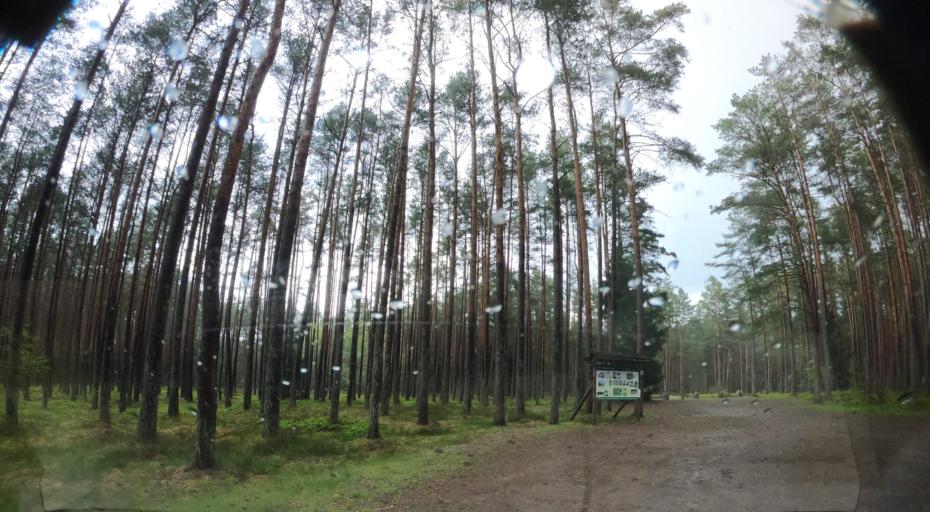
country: PL
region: West Pomeranian Voivodeship
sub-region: Powiat koszalinski
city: Bobolice
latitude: 54.0676
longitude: 16.4361
